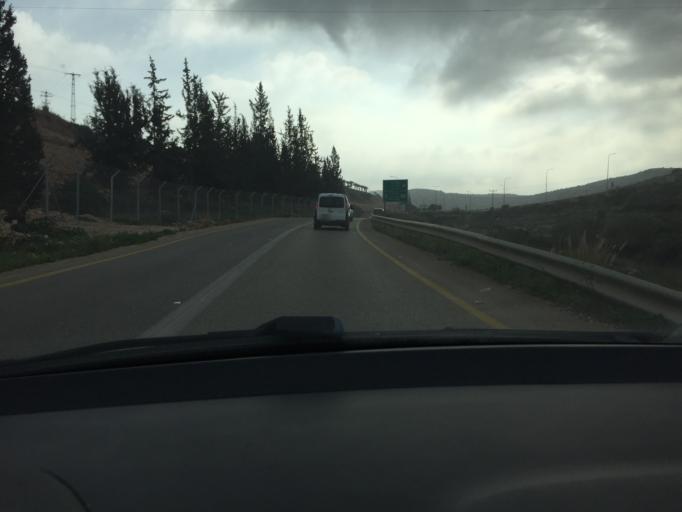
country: PS
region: West Bank
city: Al Lubban al Gharbi
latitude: 32.0352
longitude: 35.0463
